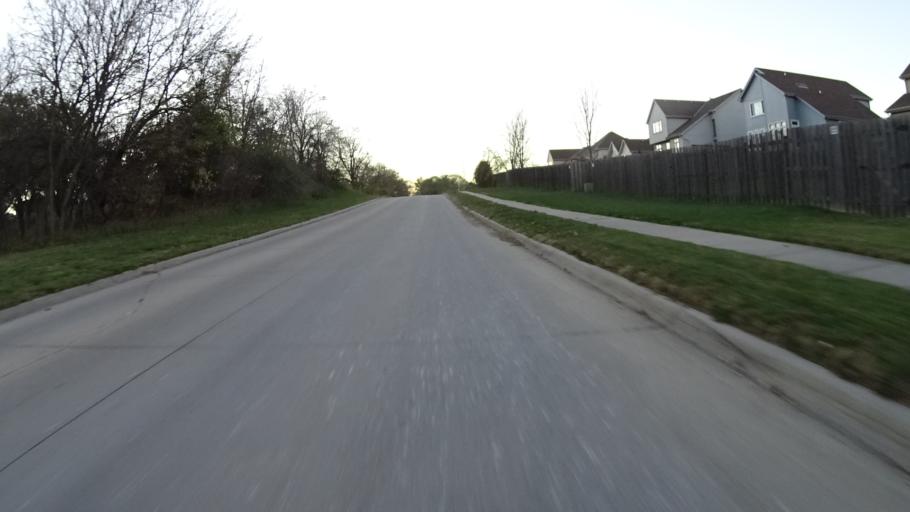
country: US
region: Nebraska
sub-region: Sarpy County
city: Offutt Air Force Base
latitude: 41.1619
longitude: -95.9531
